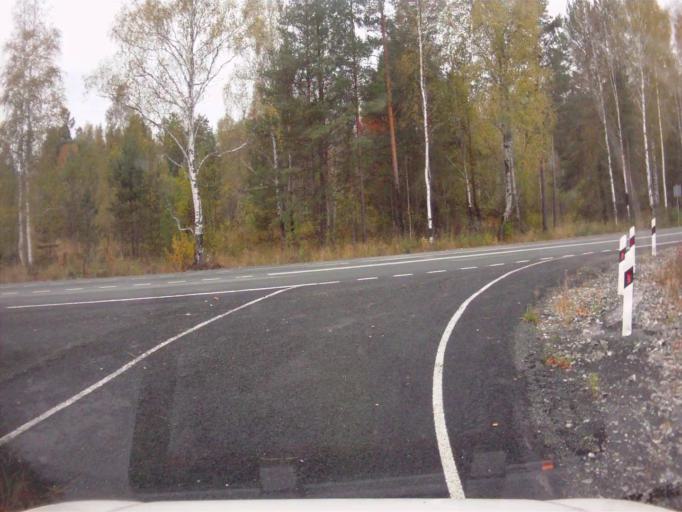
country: RU
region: Chelyabinsk
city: Nyazepetrovsk
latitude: 56.0429
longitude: 59.7765
